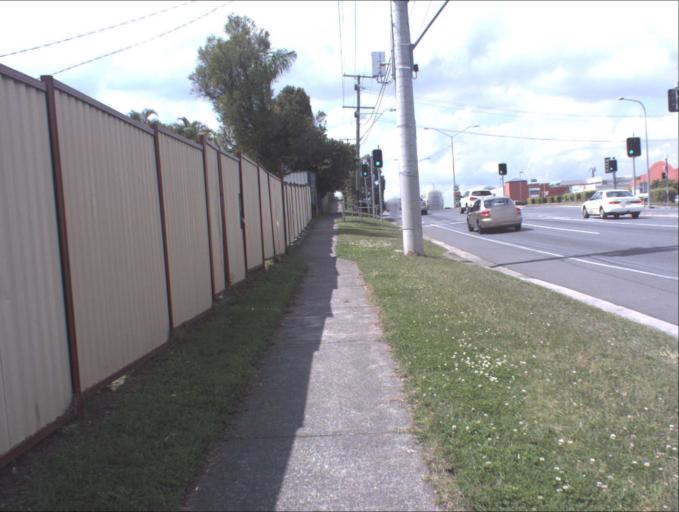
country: AU
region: Queensland
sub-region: Brisbane
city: Sunnybank Hills
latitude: -27.6616
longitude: 153.0467
